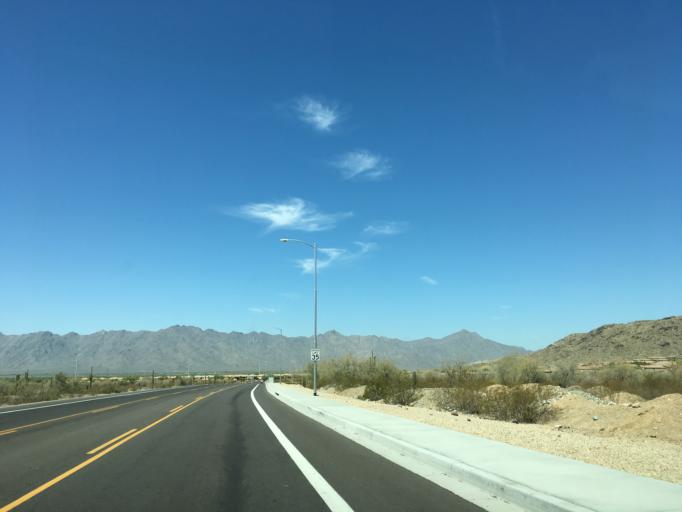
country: US
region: Arizona
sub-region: Maricopa County
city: Laveen
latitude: 33.2982
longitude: -112.1101
